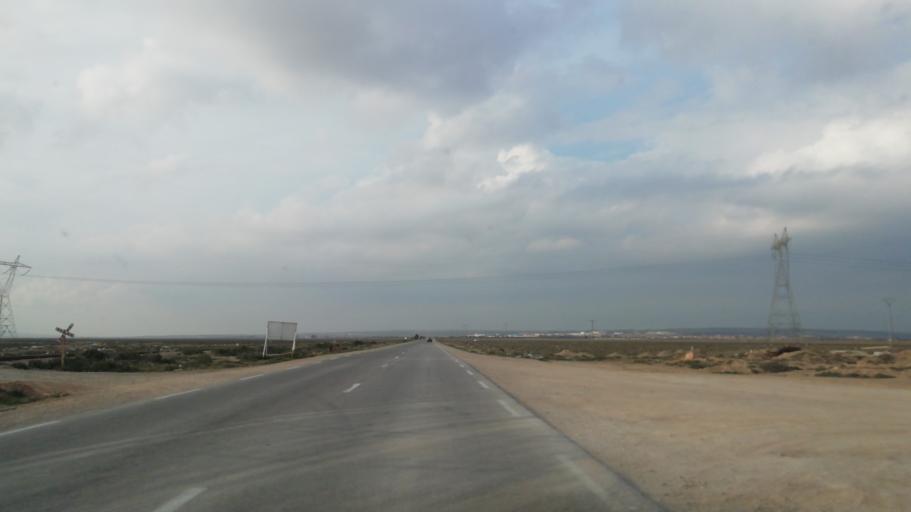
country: DZ
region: Mascara
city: Sig
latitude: 35.7028
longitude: -0.0264
